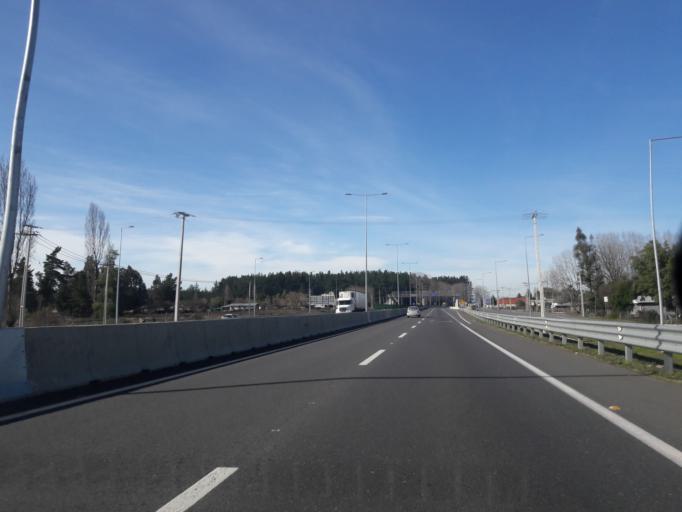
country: CL
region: Biobio
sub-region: Provincia de Biobio
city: Cabrero
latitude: -37.0309
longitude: -72.4265
